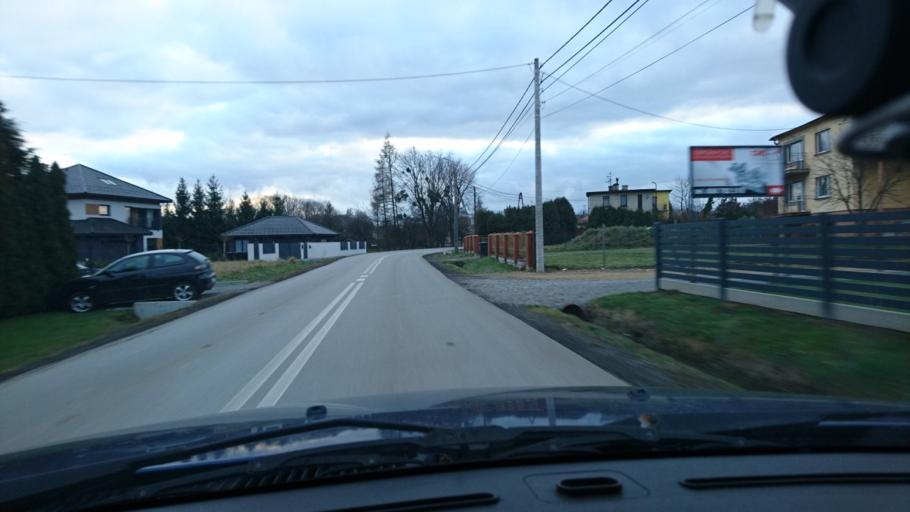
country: PL
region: Silesian Voivodeship
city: Janowice
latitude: 49.8715
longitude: 19.0958
